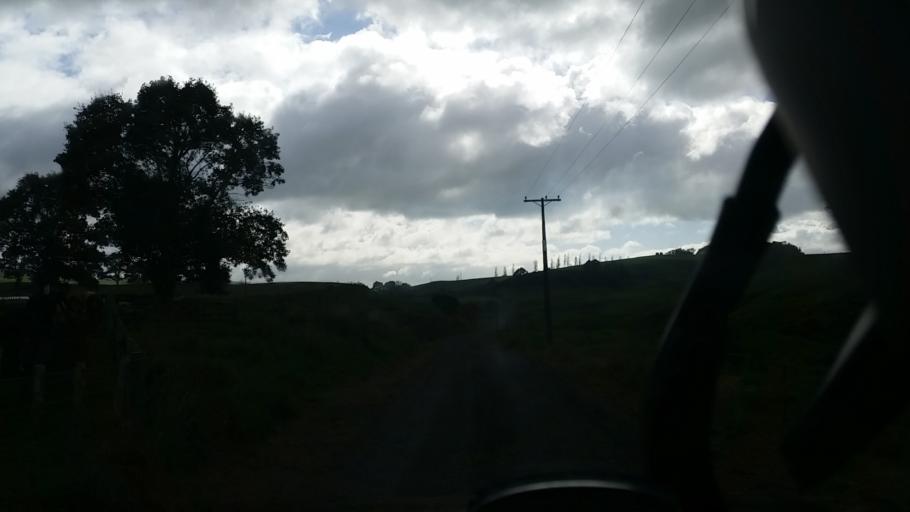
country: NZ
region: Waikato
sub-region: Matamata-Piako District
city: Matamata
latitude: -37.8156
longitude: 175.6733
